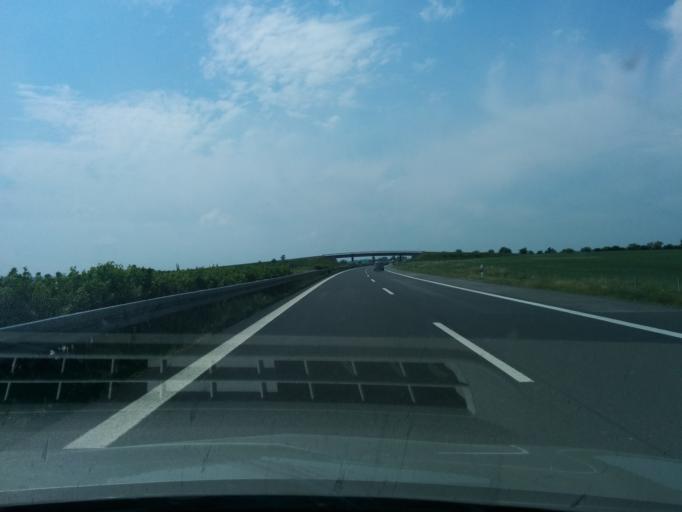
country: DE
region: Mecklenburg-Vorpommern
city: Strasburg
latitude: 53.5178
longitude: 13.8065
